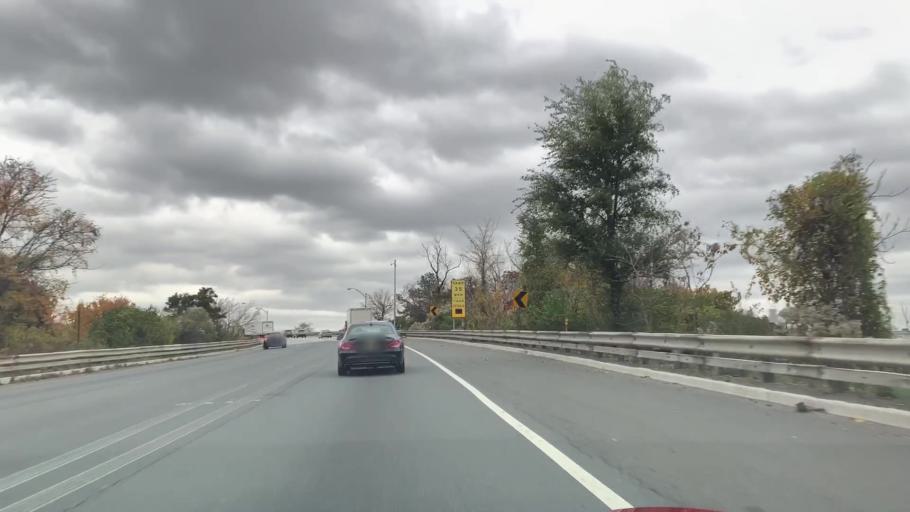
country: US
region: New Jersey
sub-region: Bergen County
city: Ridgefield Park
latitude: 40.8627
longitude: -74.0116
